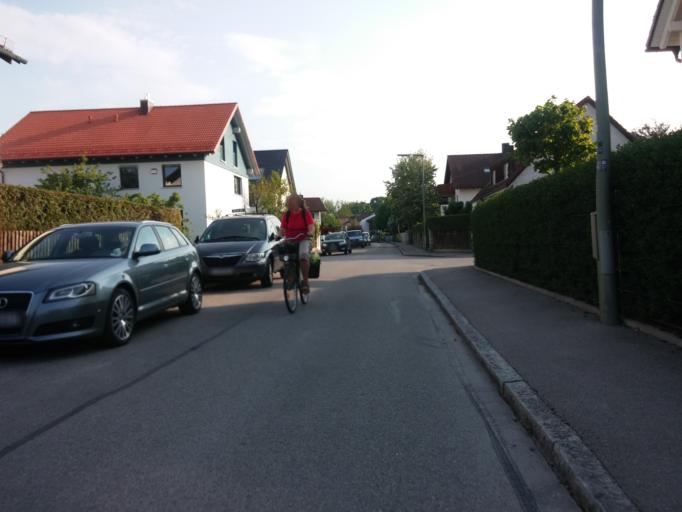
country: DE
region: Bavaria
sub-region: Upper Bavaria
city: Neubiberg
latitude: 48.1286
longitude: 11.6722
